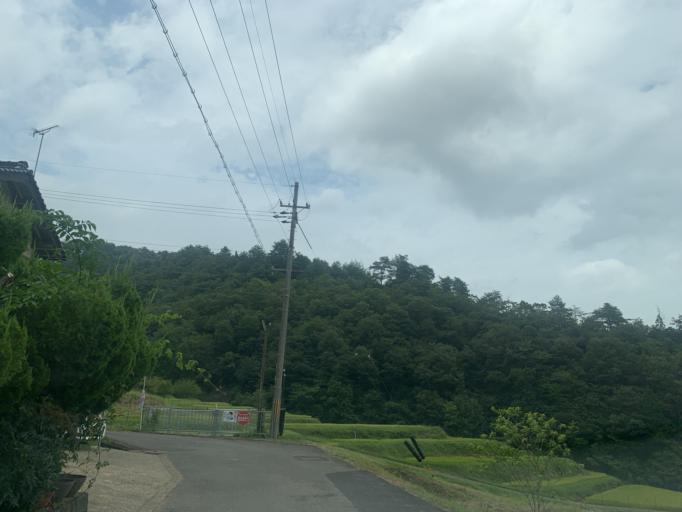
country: JP
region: Kyoto
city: Miyazu
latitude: 35.4484
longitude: 135.1613
